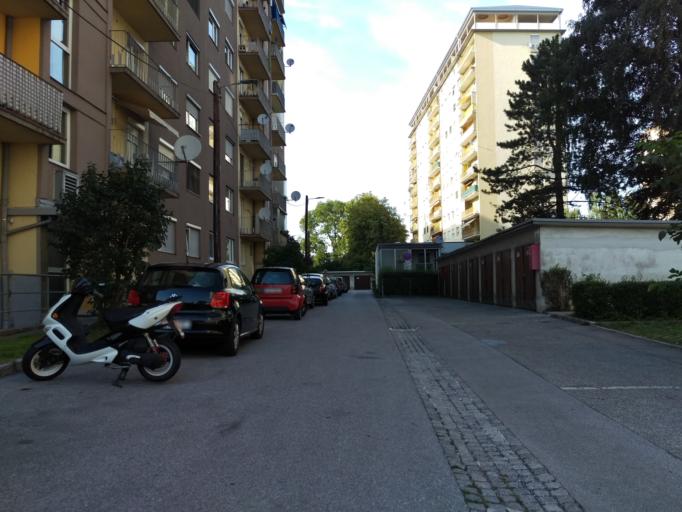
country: AT
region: Styria
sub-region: Graz Stadt
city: Graz
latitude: 47.0459
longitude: 15.4474
